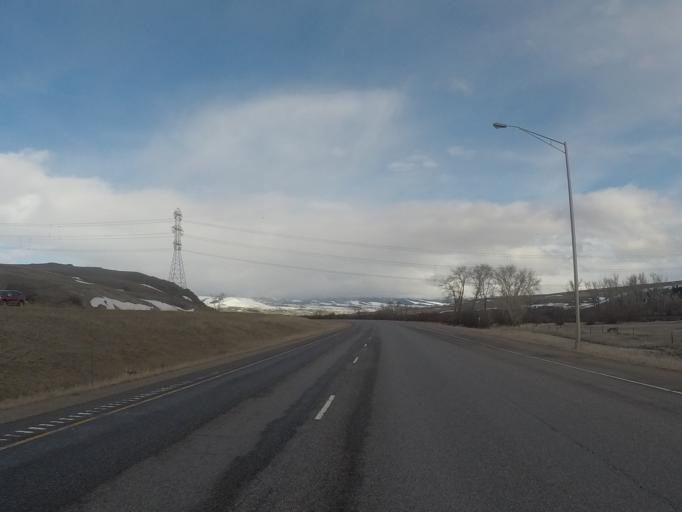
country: US
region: Montana
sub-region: Powell County
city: Deer Lodge
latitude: 46.5094
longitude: -112.7805
